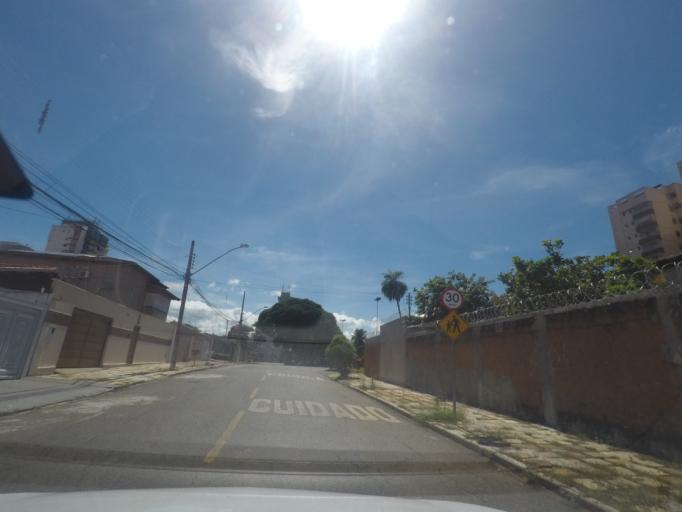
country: BR
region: Goias
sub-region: Goiania
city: Goiania
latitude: -16.6737
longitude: -49.2740
